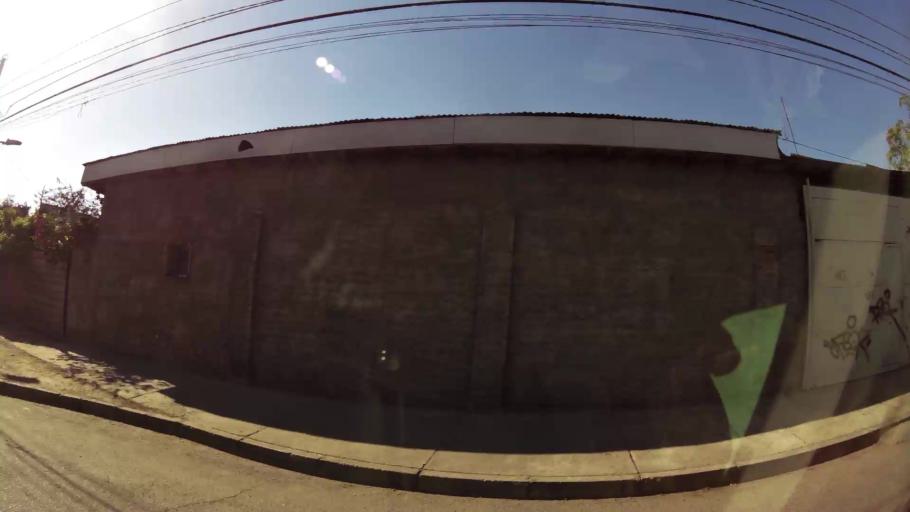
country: CL
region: Santiago Metropolitan
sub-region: Provincia de Maipo
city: San Bernardo
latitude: -33.6091
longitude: -70.6975
